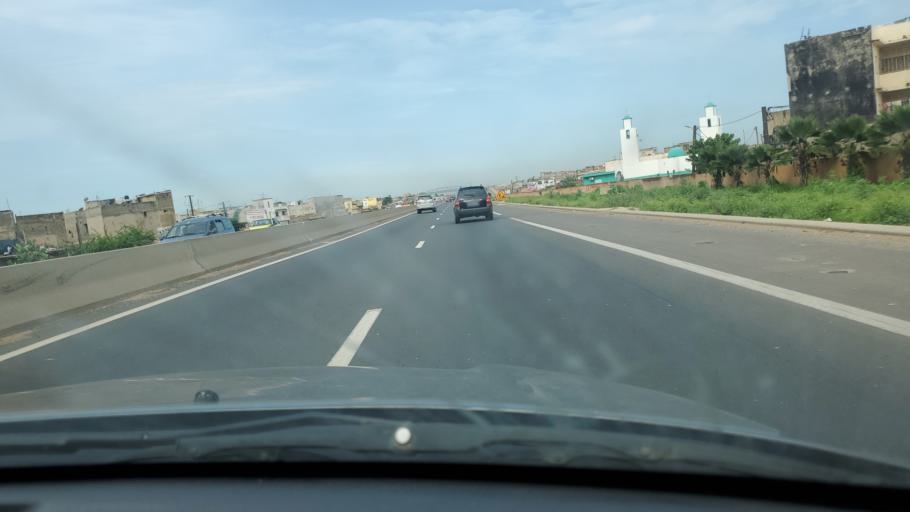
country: SN
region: Dakar
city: Pikine
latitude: 14.7574
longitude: -17.3568
